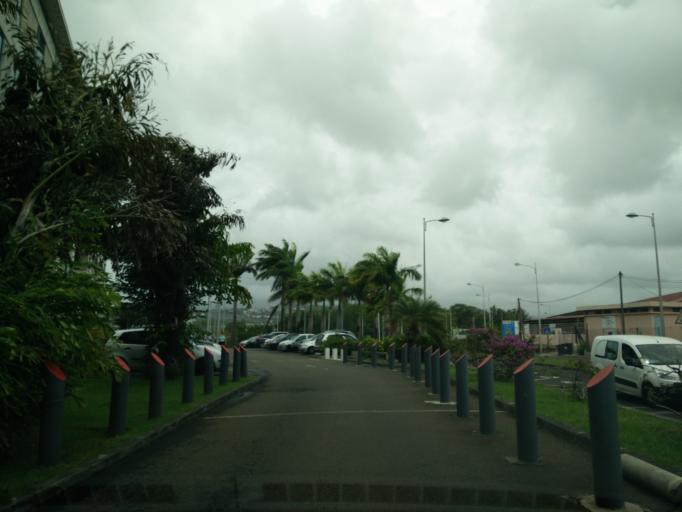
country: MQ
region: Martinique
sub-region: Martinique
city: Fort-de-France
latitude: 14.6037
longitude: -61.0421
